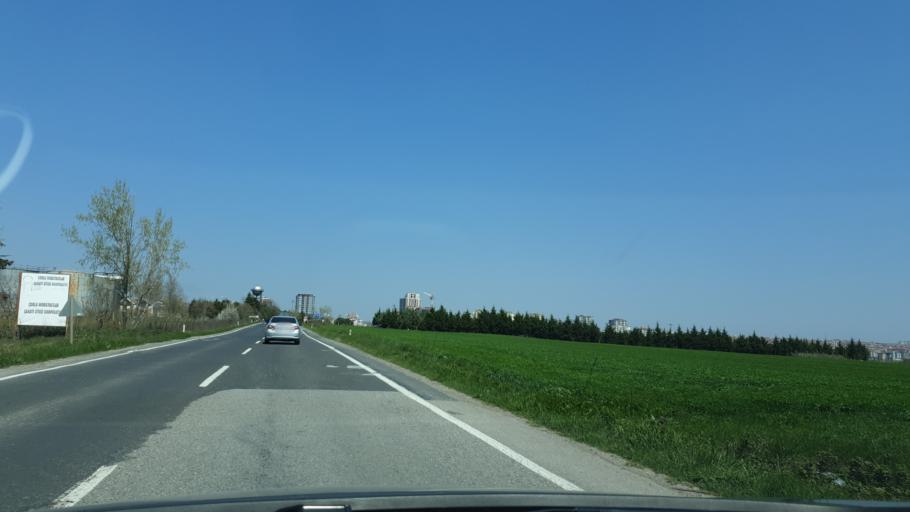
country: TR
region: Tekirdag
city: Corlu
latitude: 41.1422
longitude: 27.7695
